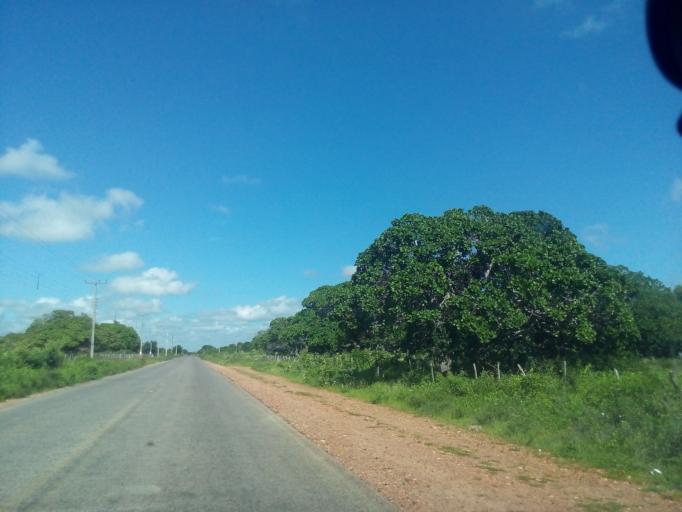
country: BR
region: Rio Grande do Norte
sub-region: Sao Paulo Do Potengi
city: Sao Paulo do Potengi
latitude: -5.9156
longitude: -35.7128
